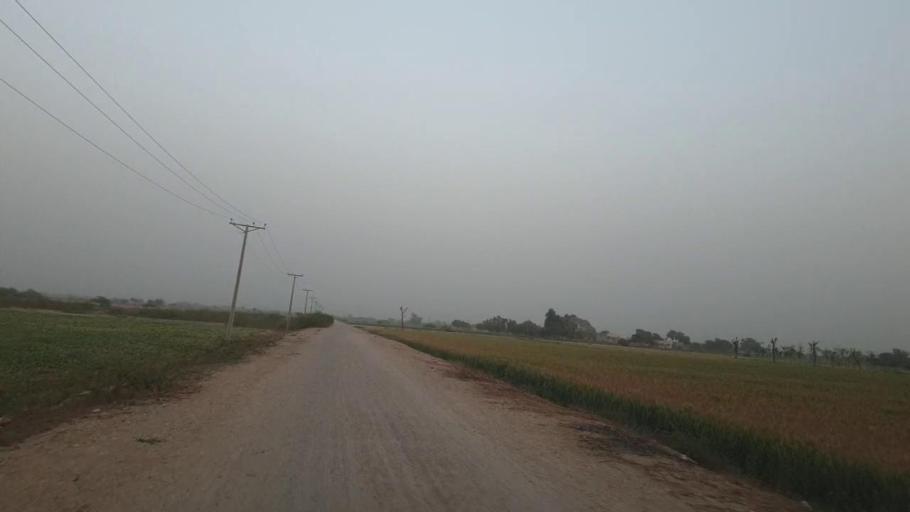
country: PK
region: Sindh
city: Kunri
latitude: 25.1221
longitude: 69.5732
